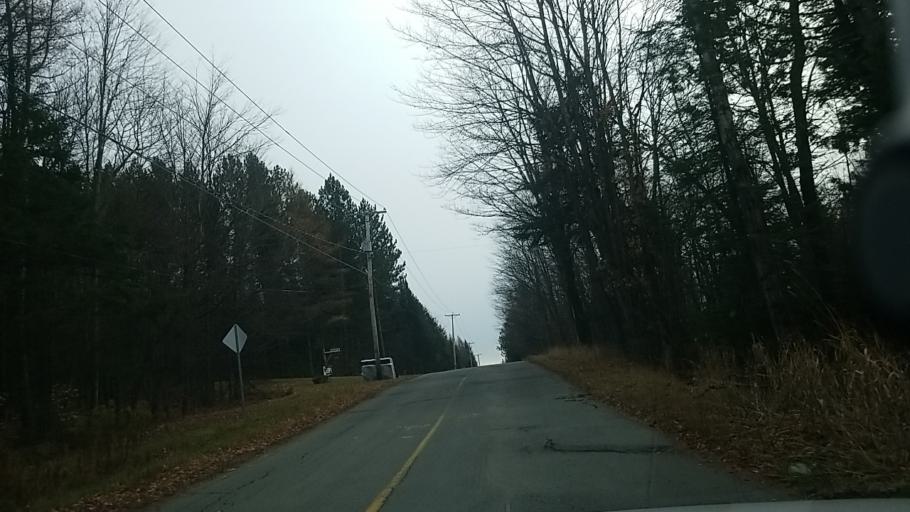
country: CA
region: Quebec
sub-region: Laurentides
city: Saint-Sauveur
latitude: 45.8220
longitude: -74.2482
